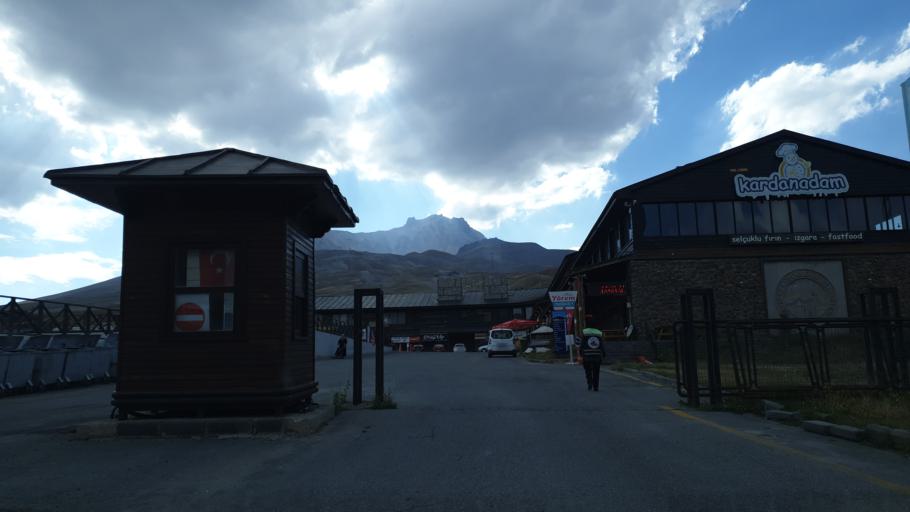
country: TR
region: Kayseri
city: Hacilar
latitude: 38.5401
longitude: 35.5279
